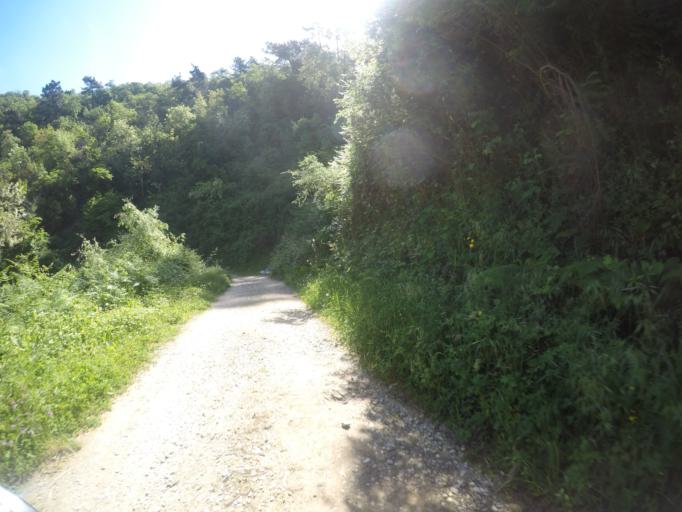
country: IT
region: Tuscany
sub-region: Provincia di Massa-Carrara
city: Massa
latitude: 44.0535
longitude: 10.1030
